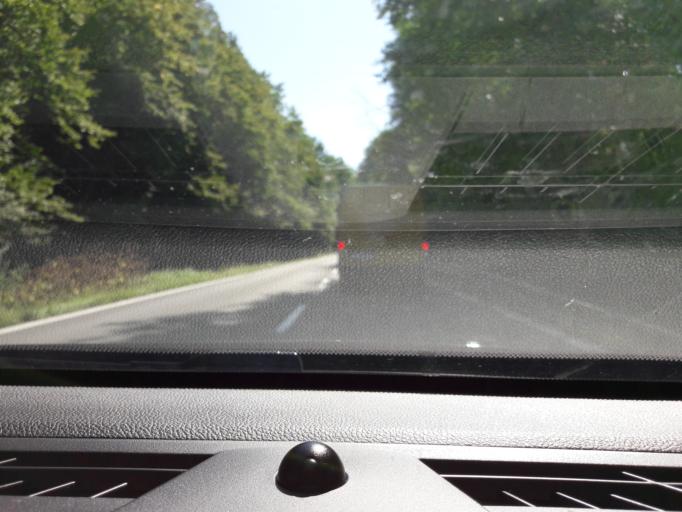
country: SK
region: Banskobystricky
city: Hrinova
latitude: 48.4931
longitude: 19.5080
